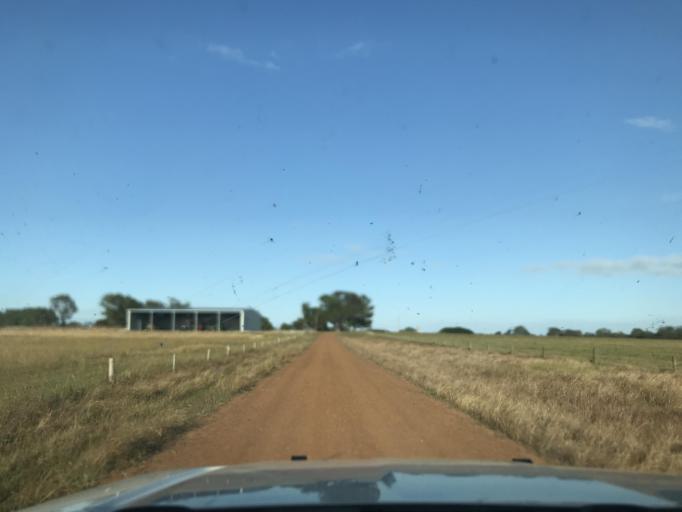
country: AU
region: South Australia
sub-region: Naracoorte and Lucindale
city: Naracoorte
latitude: -36.9550
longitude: 141.3613
